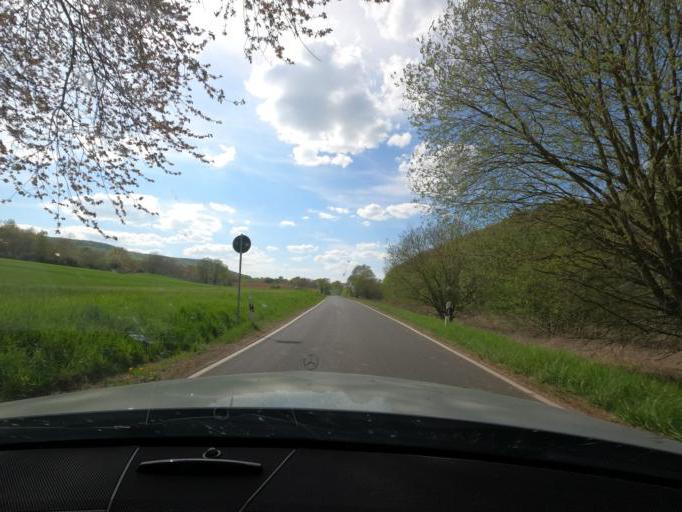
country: DE
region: Hesse
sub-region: Regierungsbezirk Kassel
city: Weissenborn
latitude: 51.1278
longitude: 10.1395
